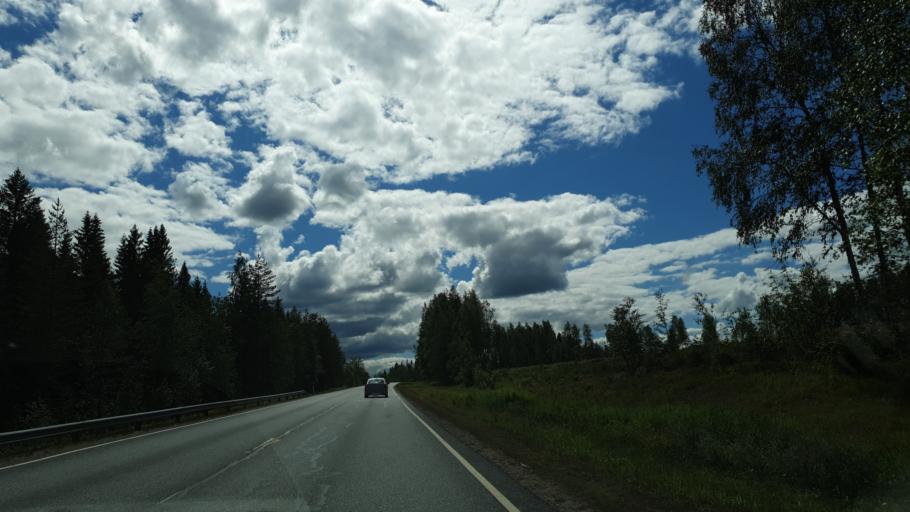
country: FI
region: North Karelia
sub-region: Pielisen Karjala
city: Valtimo
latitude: 63.4094
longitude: 28.7770
